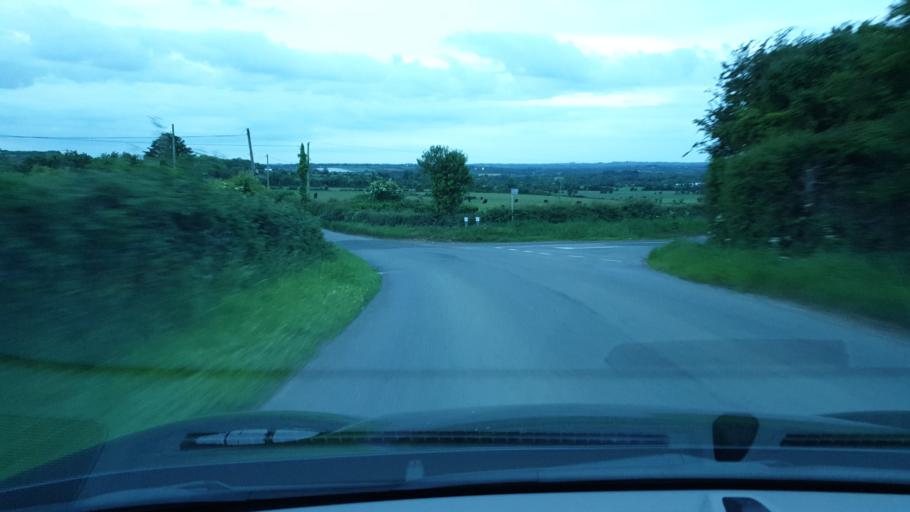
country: IE
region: Leinster
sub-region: An Mhi
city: Ashbourne
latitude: 53.5706
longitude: -6.3964
